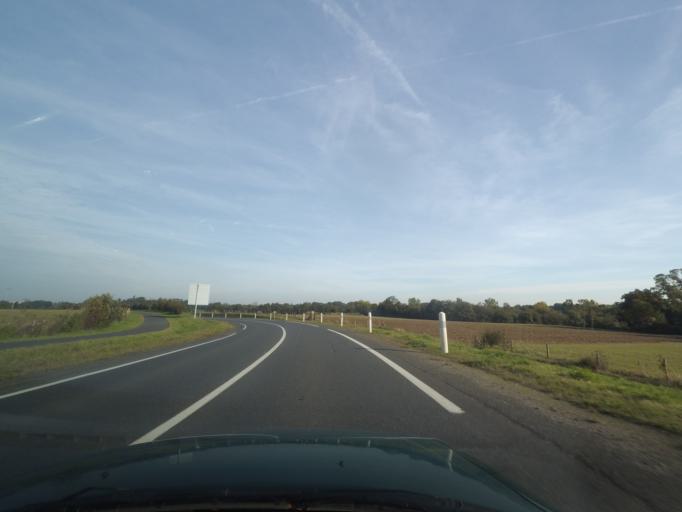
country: FR
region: Pays de la Loire
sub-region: Departement de la Vendee
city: Montaigu
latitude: 46.9683
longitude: -1.2935
